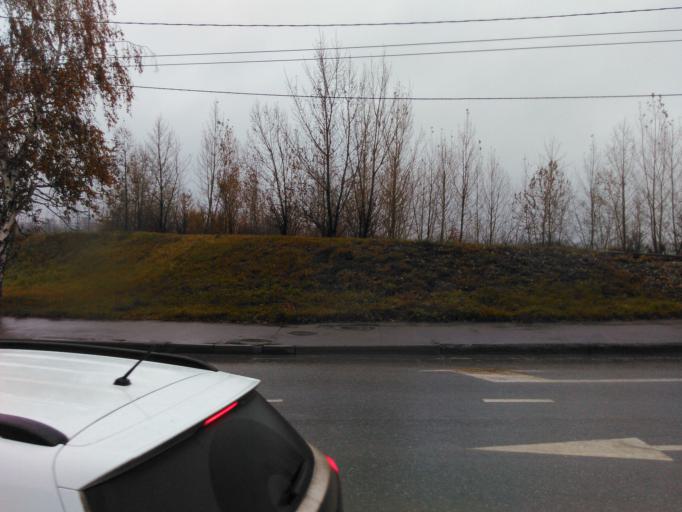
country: RU
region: Tatarstan
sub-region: Gorod Kazan'
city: Kazan
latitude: 55.8005
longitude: 49.0710
